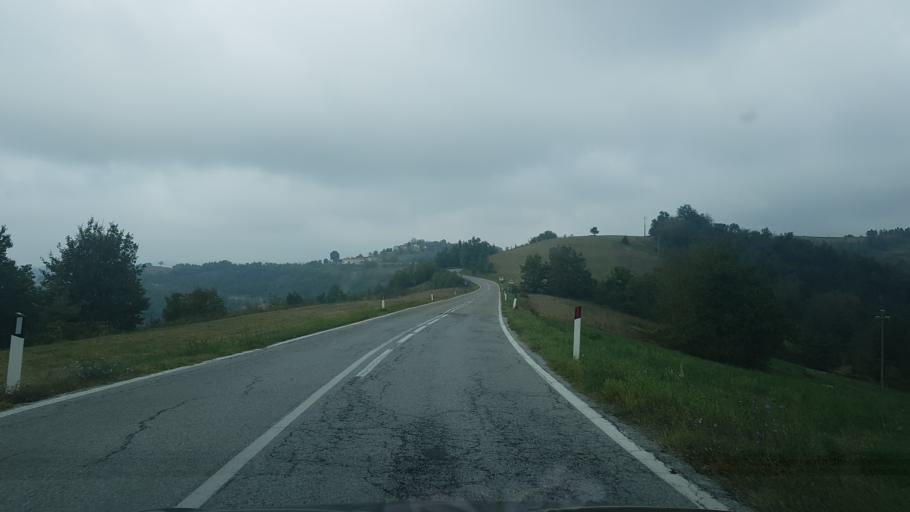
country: IT
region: Piedmont
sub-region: Provincia di Cuneo
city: Sale San Giovanni
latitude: 44.4101
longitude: 8.0959
